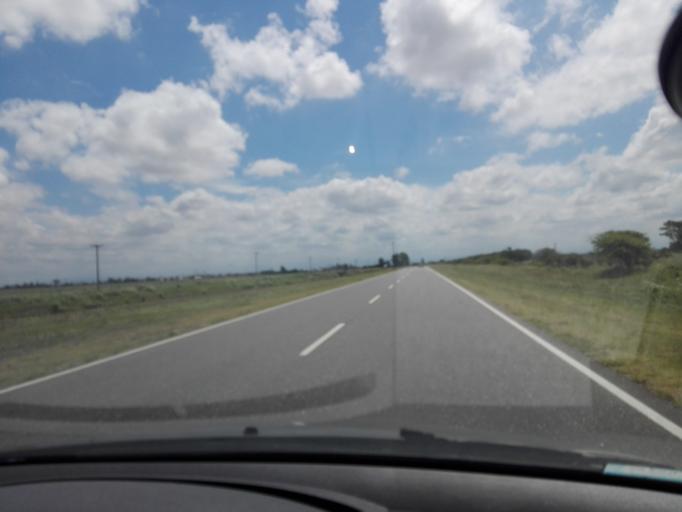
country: AR
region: Cordoba
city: Toledo
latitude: -31.6471
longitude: -64.0714
